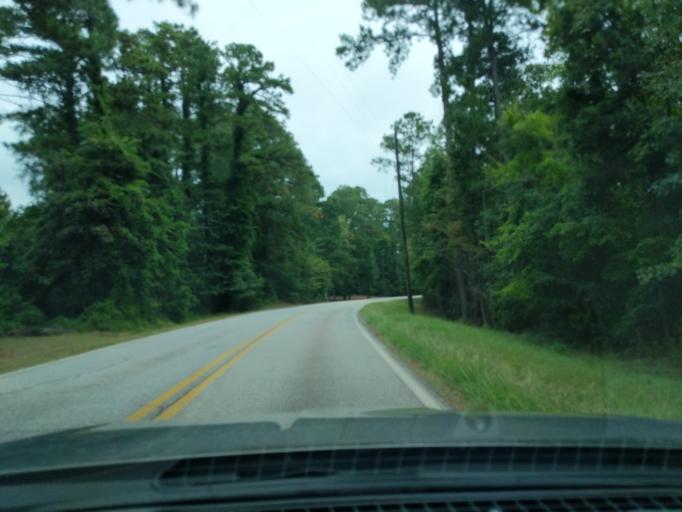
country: US
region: Georgia
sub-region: Columbia County
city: Appling
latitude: 33.5653
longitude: -82.3534
